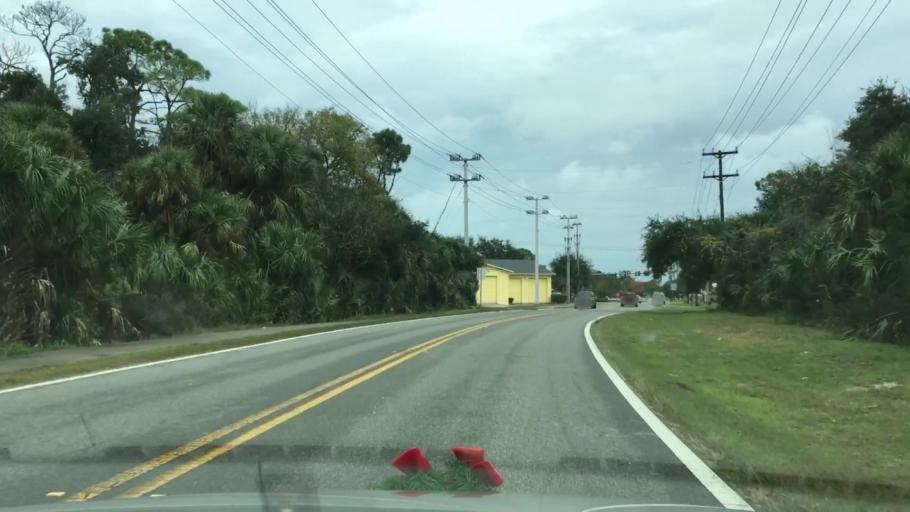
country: US
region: Florida
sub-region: Volusia County
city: Ormond Beach
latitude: 29.2898
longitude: -81.0714
